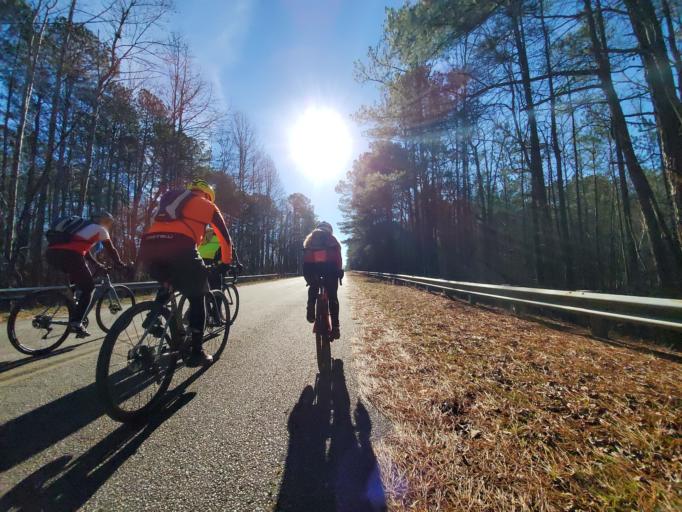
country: US
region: Georgia
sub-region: Fulton County
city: Chattahoochee Hills
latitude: 33.5695
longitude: -84.7892
